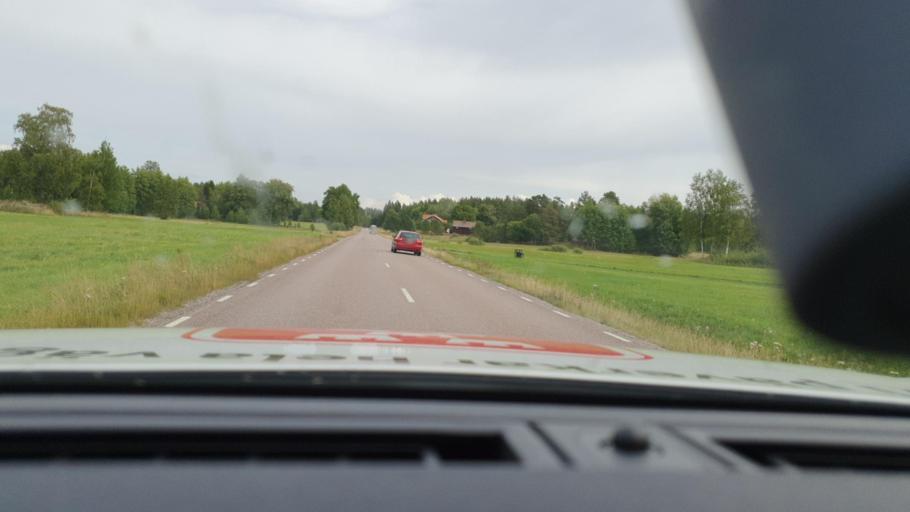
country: SE
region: Uppsala
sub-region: Heby Kommun
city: OEstervala
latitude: 60.0928
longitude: 17.0980
